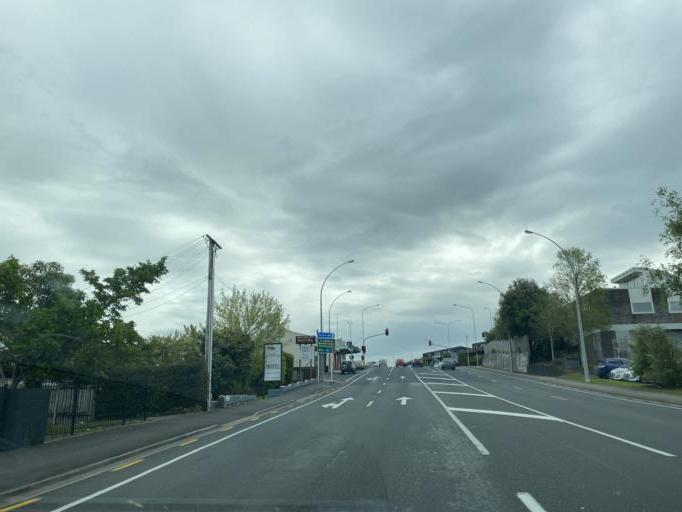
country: NZ
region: Waikato
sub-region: Hamilton City
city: Hamilton
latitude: -37.8078
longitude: 175.2817
